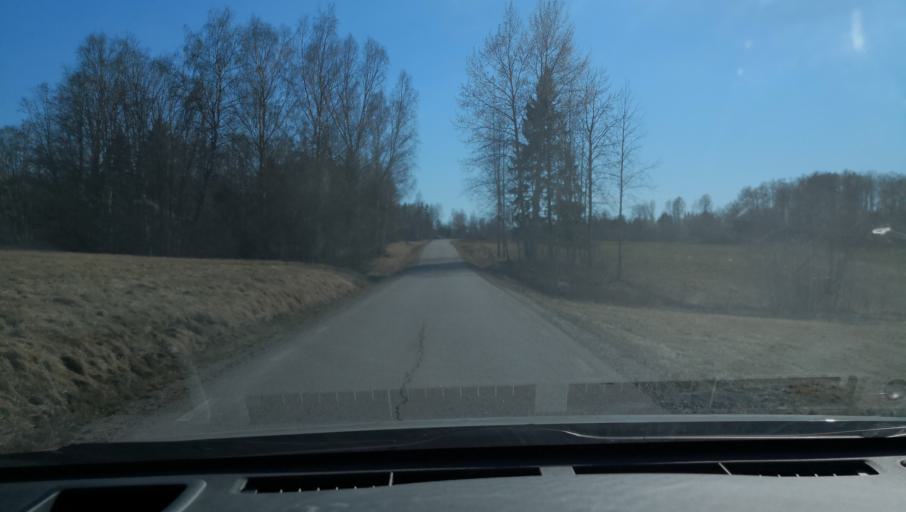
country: SE
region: Dalarna
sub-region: Avesta Kommun
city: Avesta
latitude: 60.0736
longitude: 16.3788
